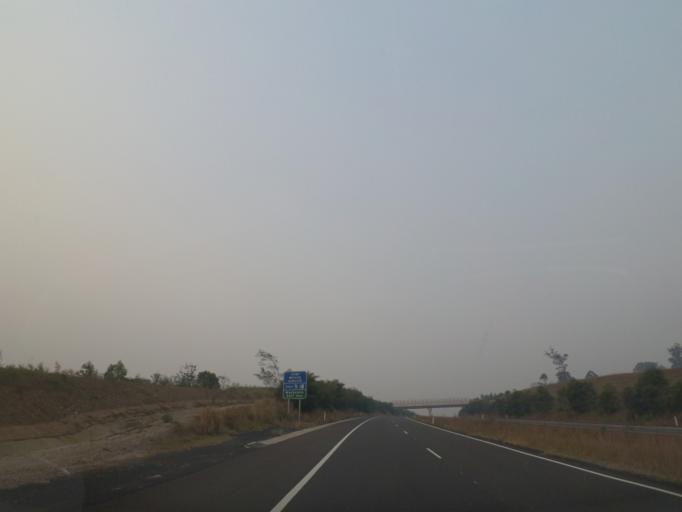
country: AU
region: New South Wales
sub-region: Nambucca Shire
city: Macksville
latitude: -30.7587
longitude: 152.9049
